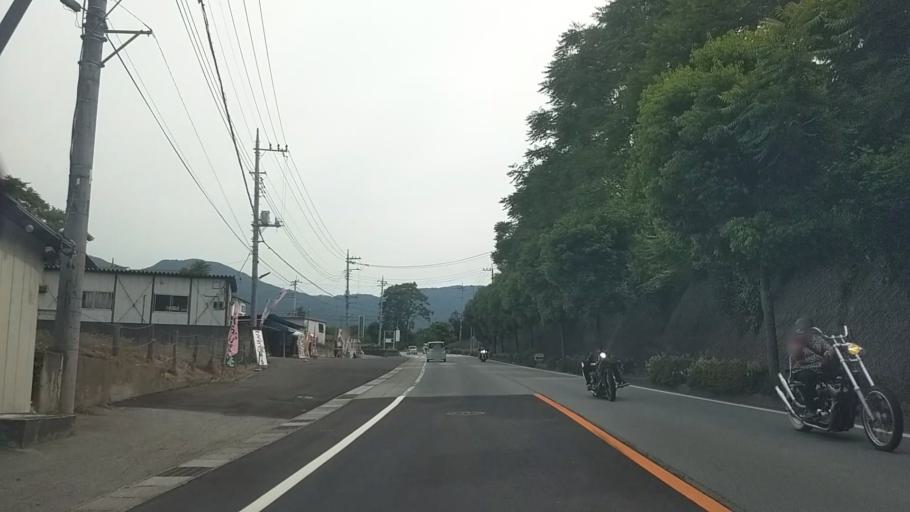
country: JP
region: Yamanashi
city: Isawa
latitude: 35.5874
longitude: 138.5902
